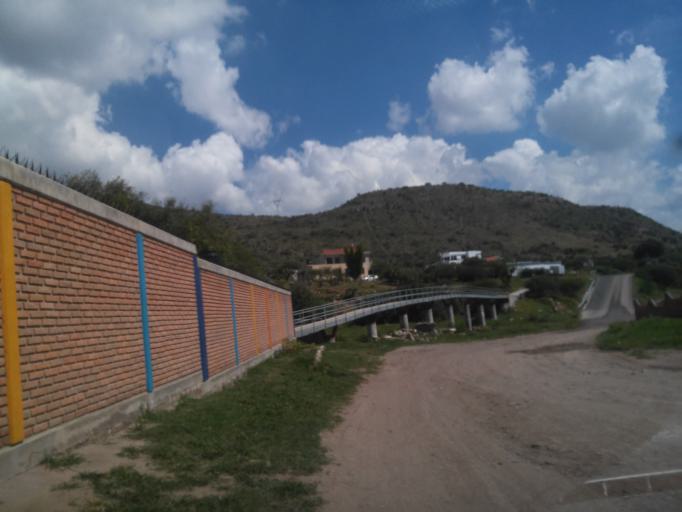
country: MX
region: Durango
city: Victoria de Durango
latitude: 24.0129
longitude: -104.7389
